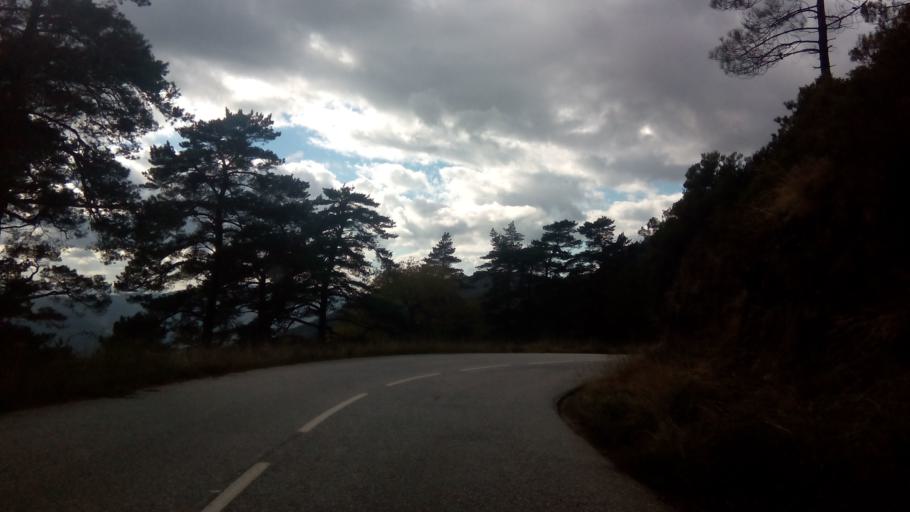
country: PT
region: Vila Real
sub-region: Mesao Frio
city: Mesao Frio
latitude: 41.2781
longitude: -7.9260
